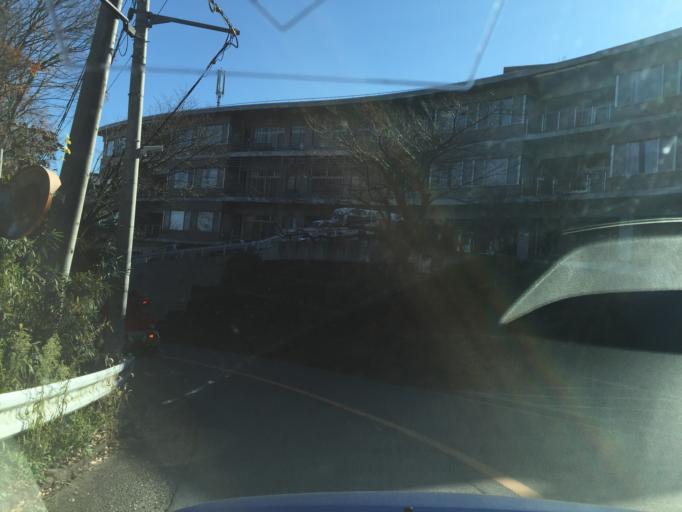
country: JP
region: Nara
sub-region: Ikoma-shi
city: Ikoma
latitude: 34.6871
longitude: 135.6890
